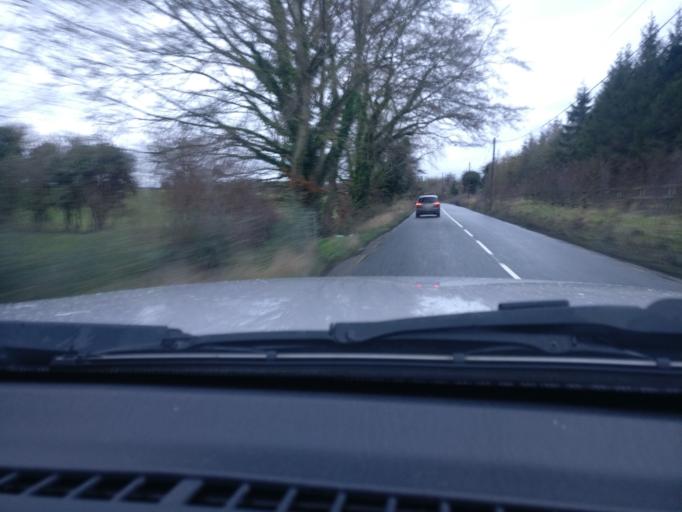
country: IE
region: Leinster
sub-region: An Mhi
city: Longwood
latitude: 53.4871
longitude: -6.8854
